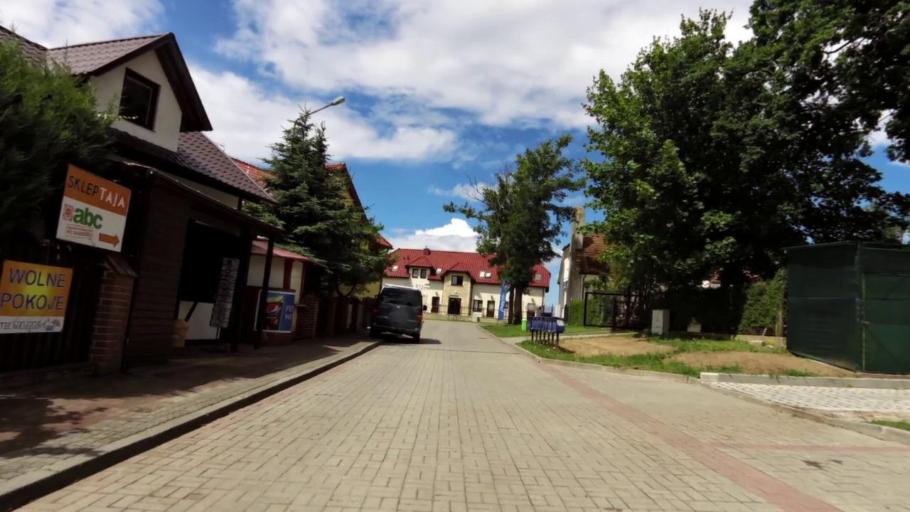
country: PL
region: West Pomeranian Voivodeship
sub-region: Powiat slawienski
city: Darlowo
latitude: 54.5381
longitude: 16.5282
